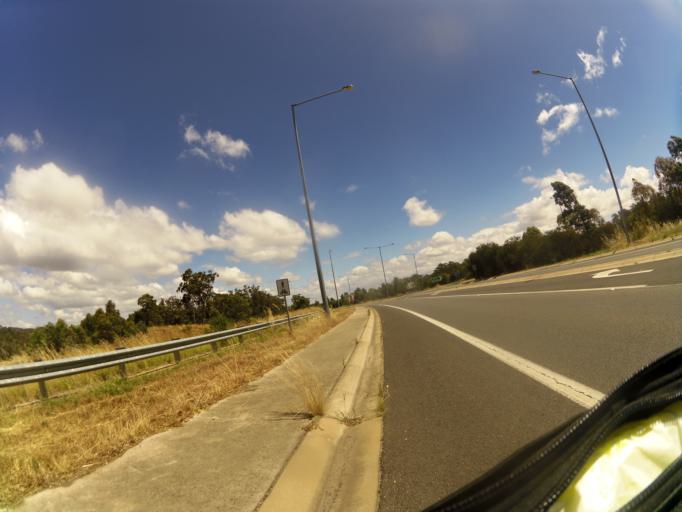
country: AU
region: Victoria
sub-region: Mount Alexander
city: Castlemaine
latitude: -37.0044
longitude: 144.2486
